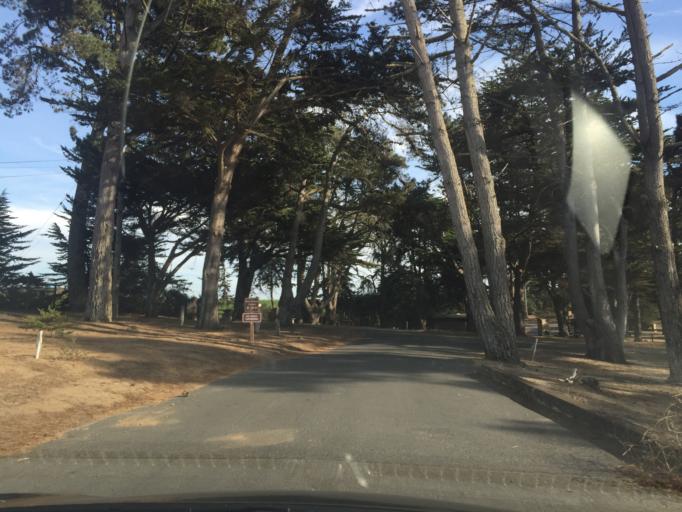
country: US
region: California
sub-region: Santa Cruz County
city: La Selva Beach
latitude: 36.8891
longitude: -121.8300
